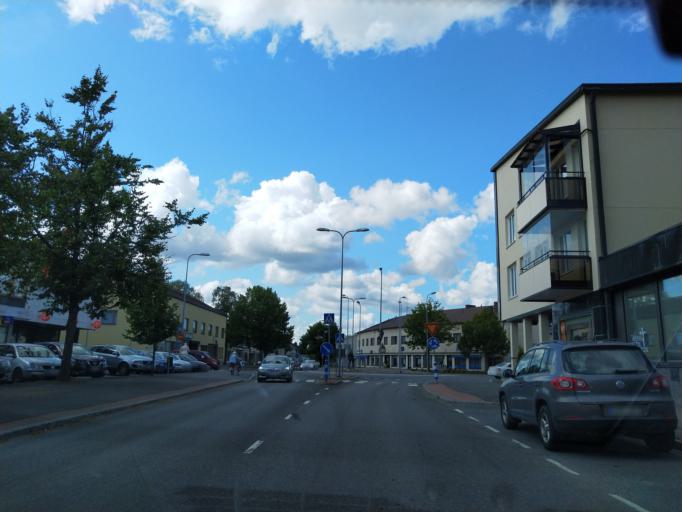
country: FI
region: Satakunta
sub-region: Pori
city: Huittinen
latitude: 61.1764
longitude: 22.6991
